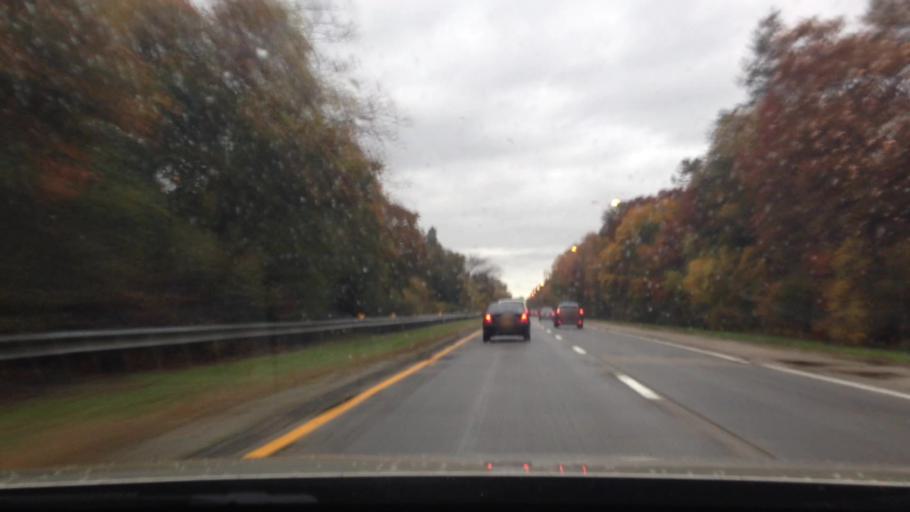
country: US
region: New York
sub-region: Suffolk County
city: Bay Wood
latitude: 40.7572
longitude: -73.2798
